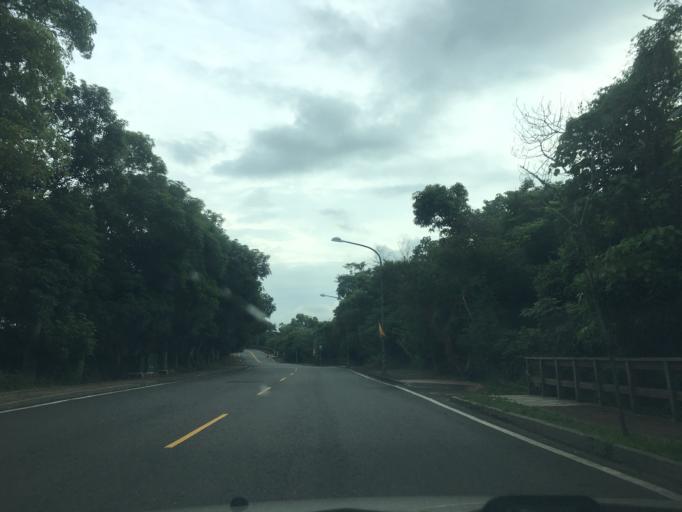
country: TW
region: Taiwan
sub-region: Changhua
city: Chang-hua
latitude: 24.0695
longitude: 120.5651
